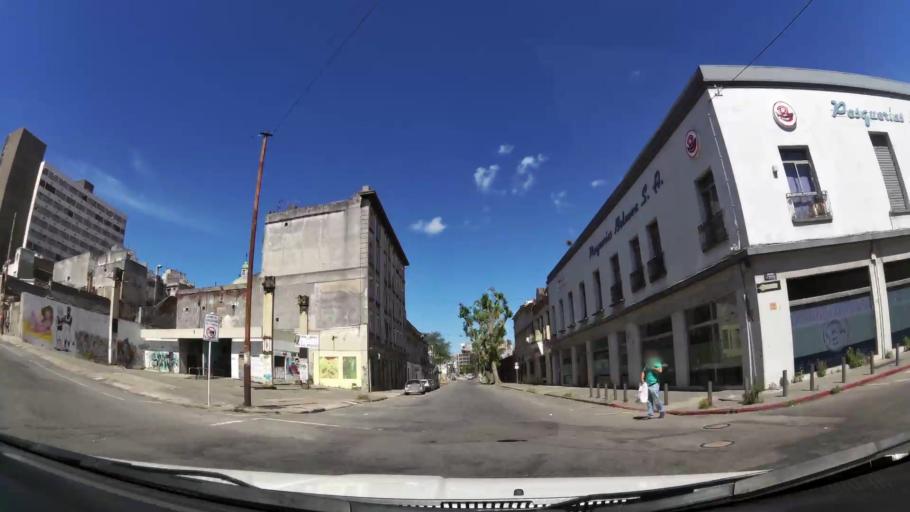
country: UY
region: Montevideo
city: Montevideo
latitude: -34.9023
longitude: -56.2009
